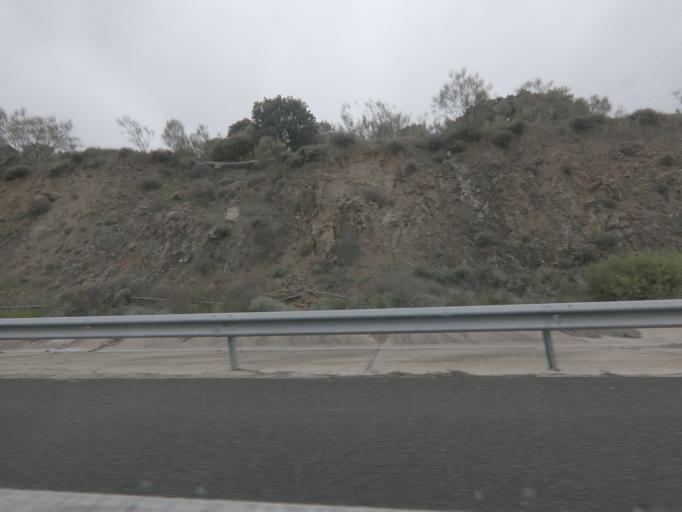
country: ES
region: Extremadura
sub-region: Provincia de Caceres
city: Plasencia
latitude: 40.0167
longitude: -6.1292
